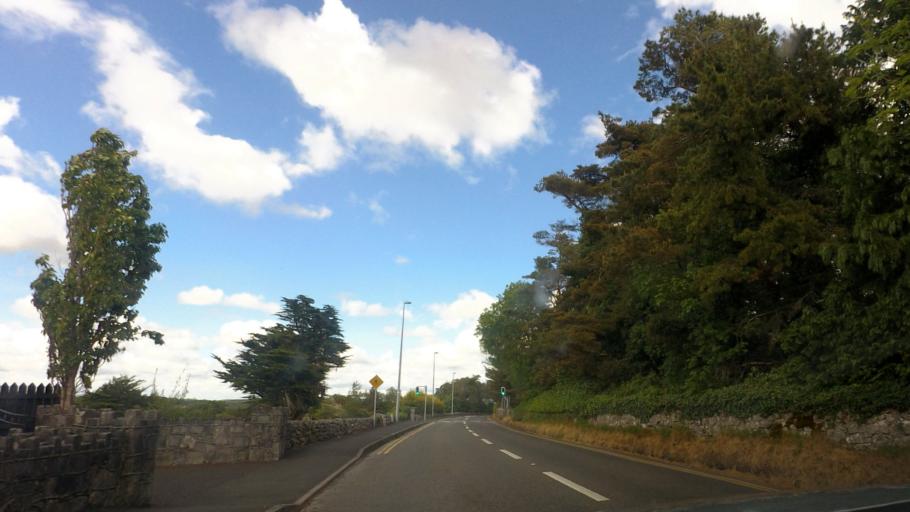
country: IE
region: Munster
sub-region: An Clar
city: Ennis
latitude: 52.8385
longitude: -9.0043
